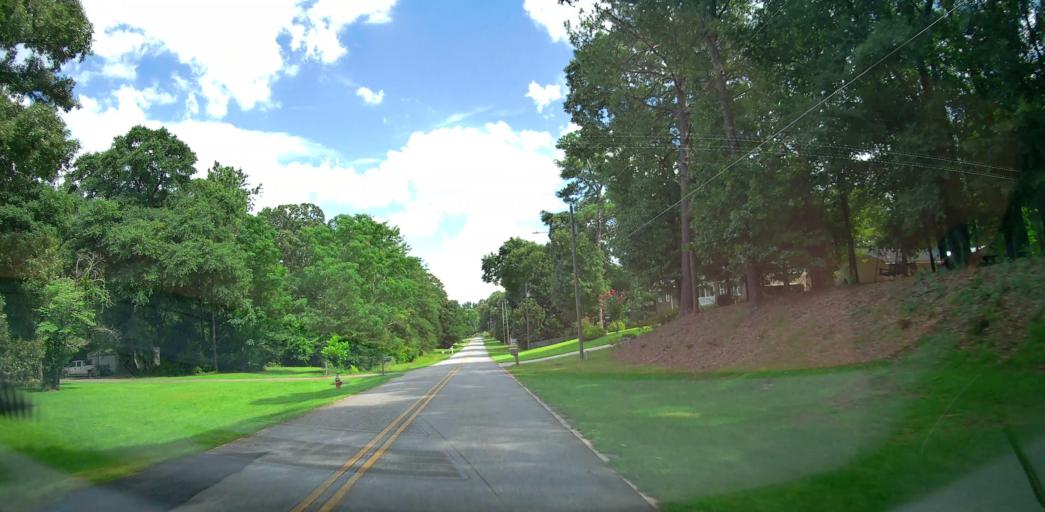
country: US
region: Georgia
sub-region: Houston County
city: Centerville
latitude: 32.5800
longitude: -83.6659
